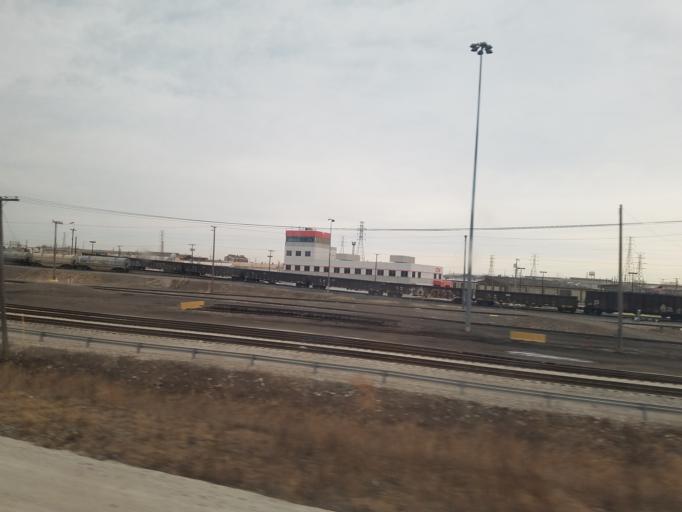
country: US
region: Indiana
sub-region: Lake County
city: Gary
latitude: 41.6104
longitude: -87.3537
